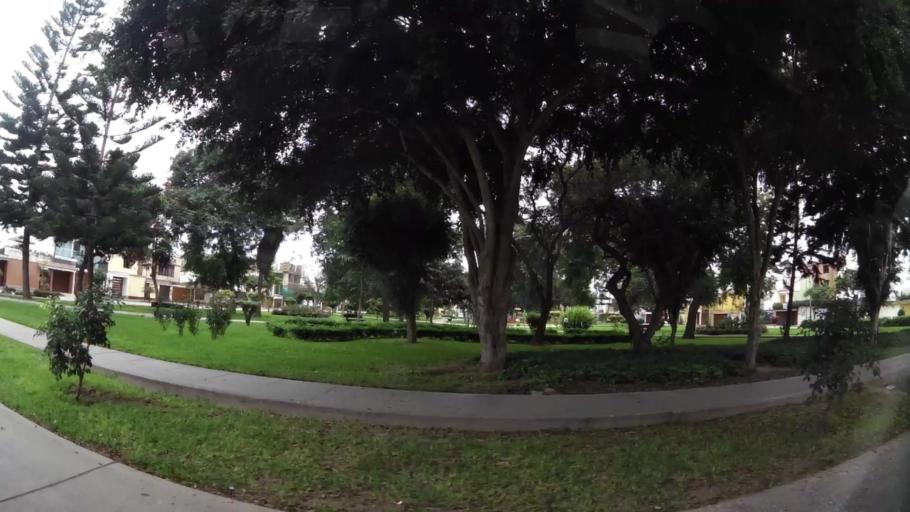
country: PE
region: Lima
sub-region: Lima
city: Surco
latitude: -12.1381
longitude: -76.9971
